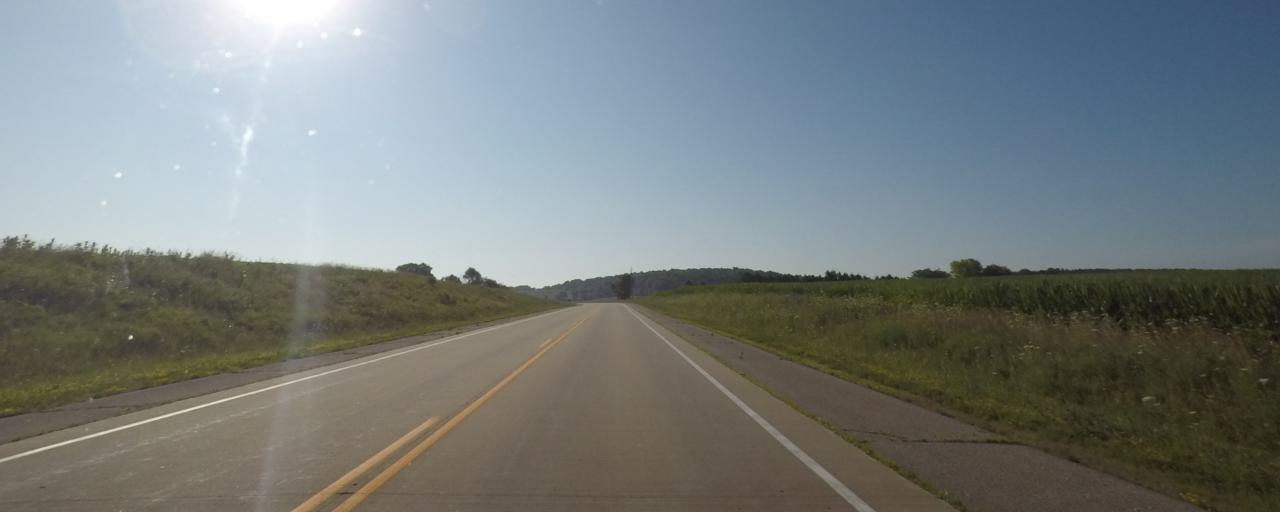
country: US
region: Wisconsin
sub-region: Jefferson County
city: Lake Ripley
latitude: 42.9752
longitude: -88.9505
